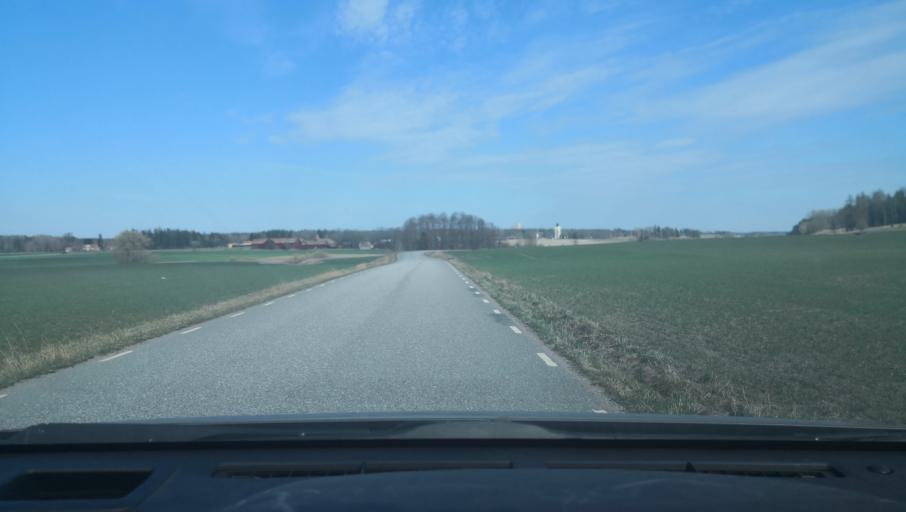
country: SE
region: Uppsala
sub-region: Enkopings Kommun
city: Irsta
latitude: 59.7705
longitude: 16.8717
